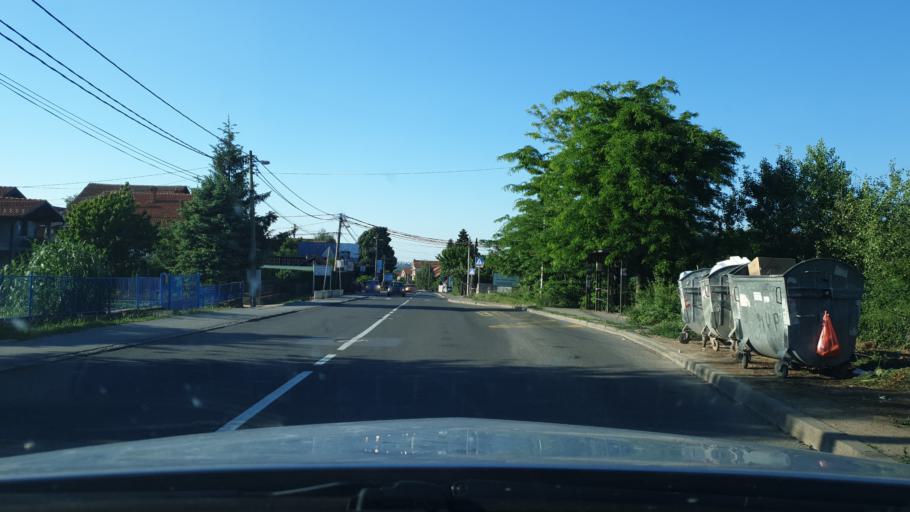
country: RS
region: Central Serbia
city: Sremcica
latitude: 44.7138
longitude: 20.3681
